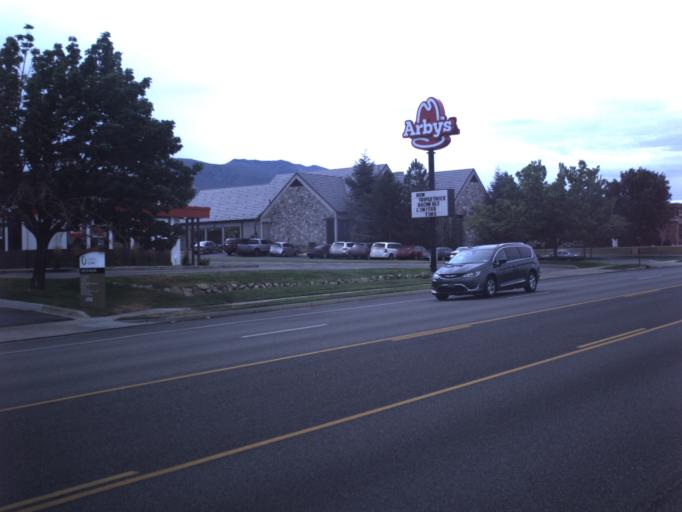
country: US
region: Utah
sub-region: Weber County
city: South Ogden
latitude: 41.1776
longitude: -111.9493
